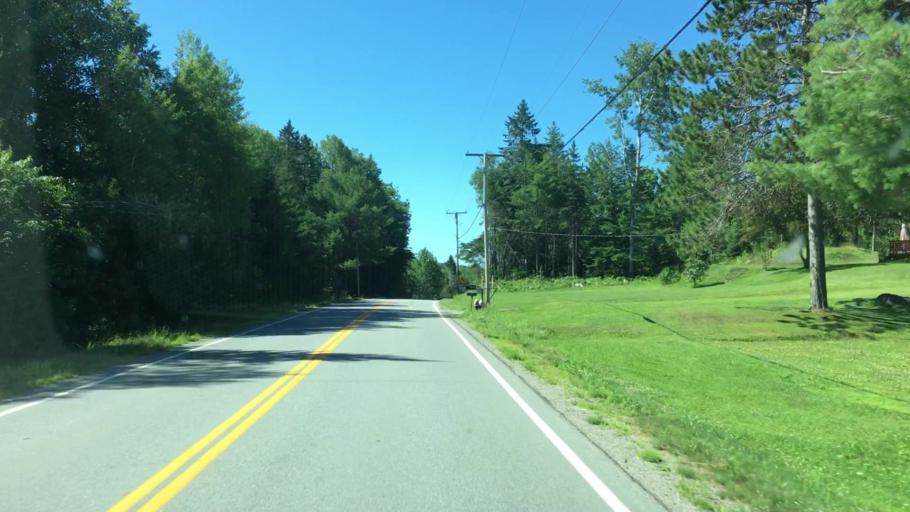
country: US
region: Maine
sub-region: Hancock County
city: Dedham
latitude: 44.7083
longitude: -68.6501
